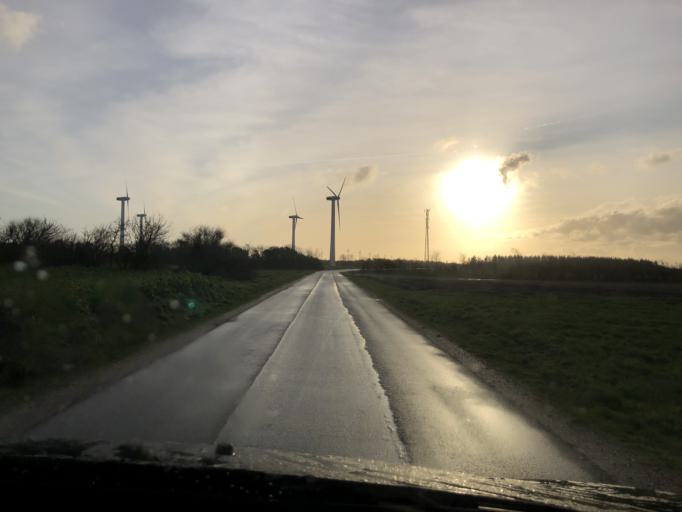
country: DK
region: Central Jutland
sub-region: Ringkobing-Skjern Kommune
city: Skjern
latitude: 55.8686
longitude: 8.3607
